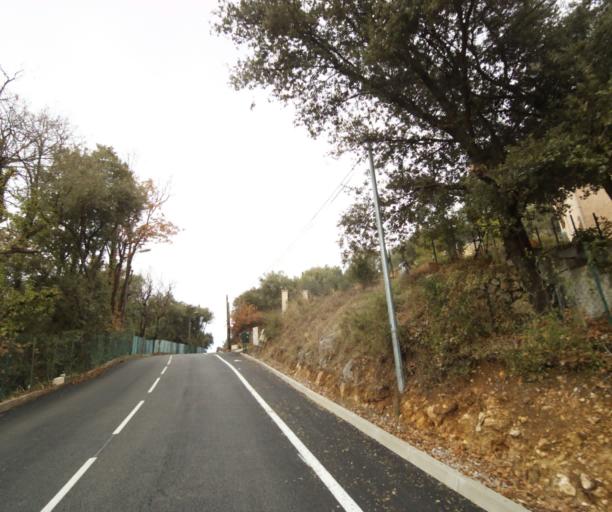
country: FR
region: Provence-Alpes-Cote d'Azur
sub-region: Departement du Var
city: Trans-en-Provence
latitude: 43.5070
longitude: 6.4859
